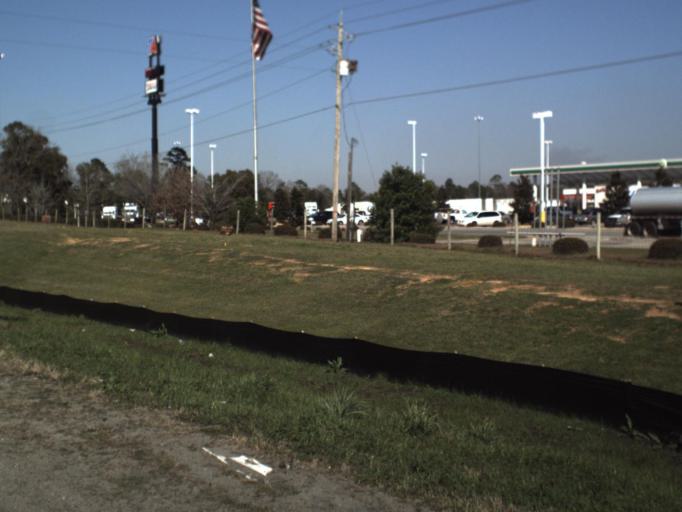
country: US
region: Florida
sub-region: Jackson County
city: Marianna
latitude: 30.7180
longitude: -85.1853
